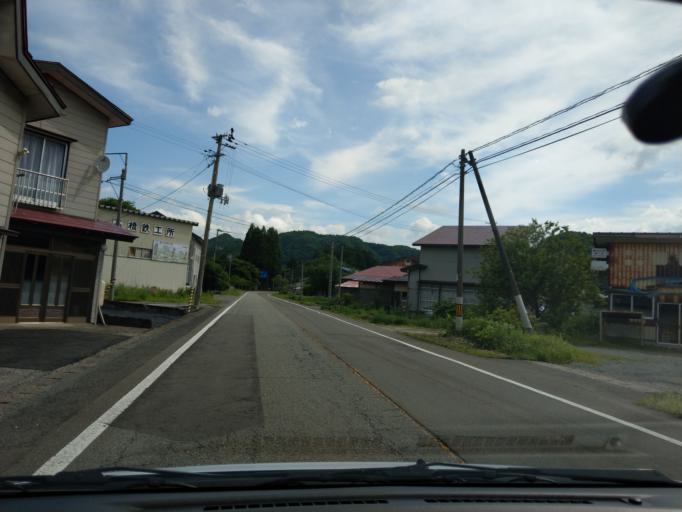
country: JP
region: Akita
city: Kakunodatemachi
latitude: 39.7442
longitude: 140.5927
